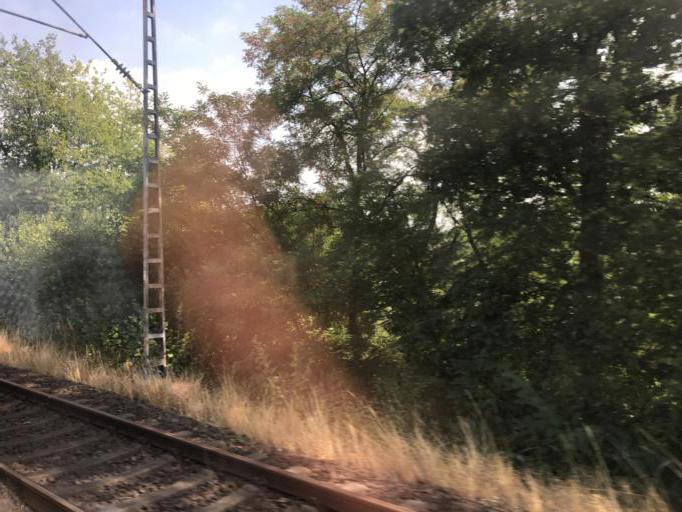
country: DE
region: Saarland
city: Neunkirchen
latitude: 49.3654
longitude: 7.1729
